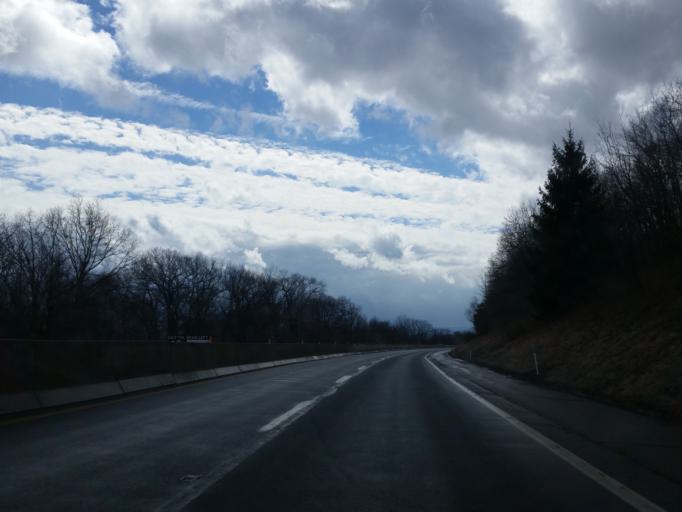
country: US
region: Pennsylvania
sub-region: Lackawanna County
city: Taylor
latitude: 41.4327
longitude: -75.7035
